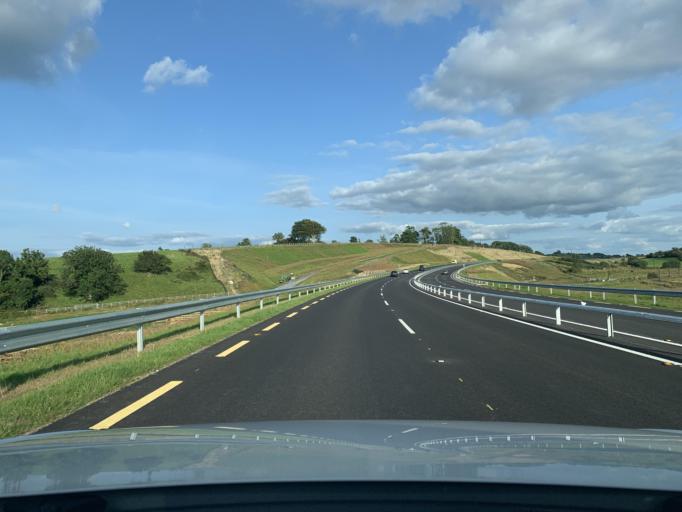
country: IE
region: Connaught
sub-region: Sligo
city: Ballymote
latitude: 54.1009
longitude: -8.3996
